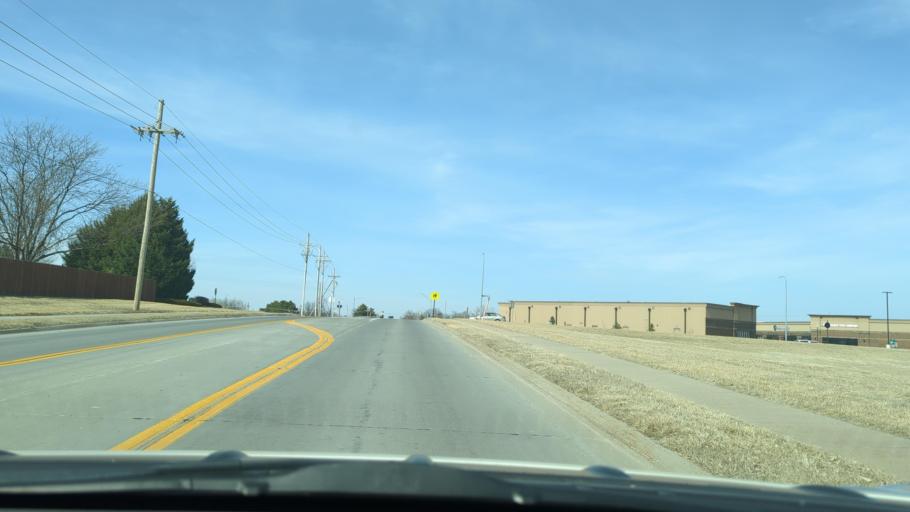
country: US
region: Nebraska
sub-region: Sarpy County
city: Papillion
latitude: 41.1375
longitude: -96.0524
